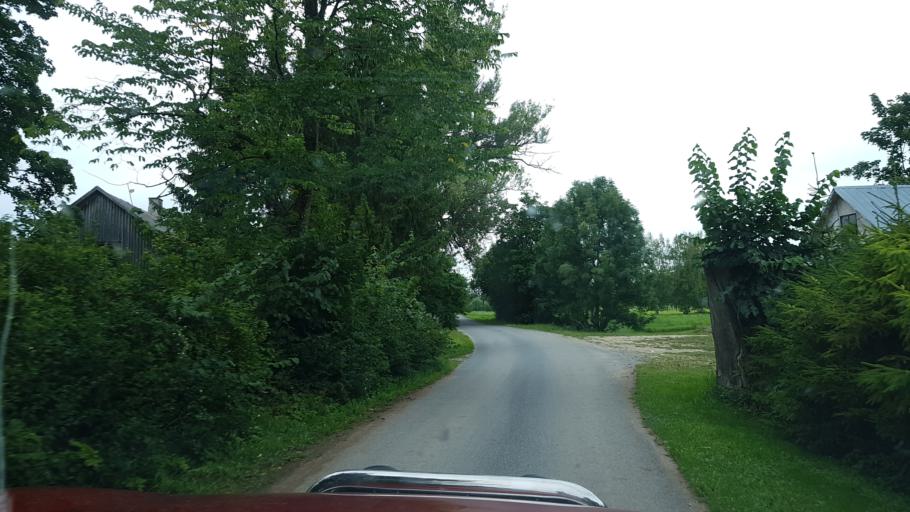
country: EE
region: Laeaene
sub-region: Ridala Parish
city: Uuemoisa
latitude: 58.7883
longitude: 23.6628
